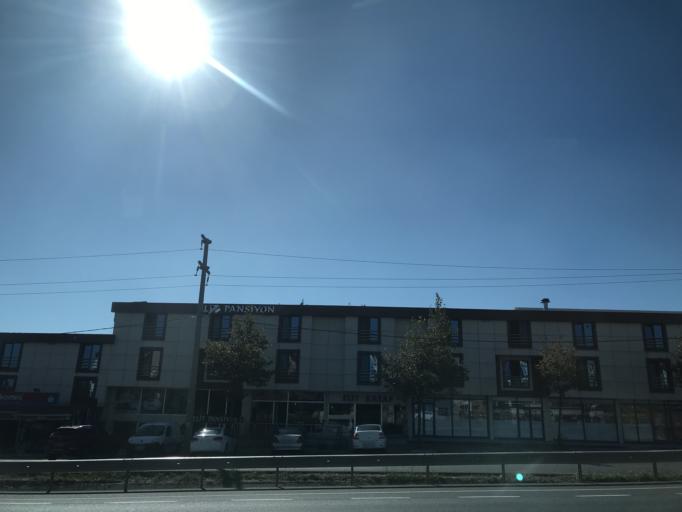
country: TR
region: Tekirdag
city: Sultankoy
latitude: 41.0475
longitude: 28.0469
